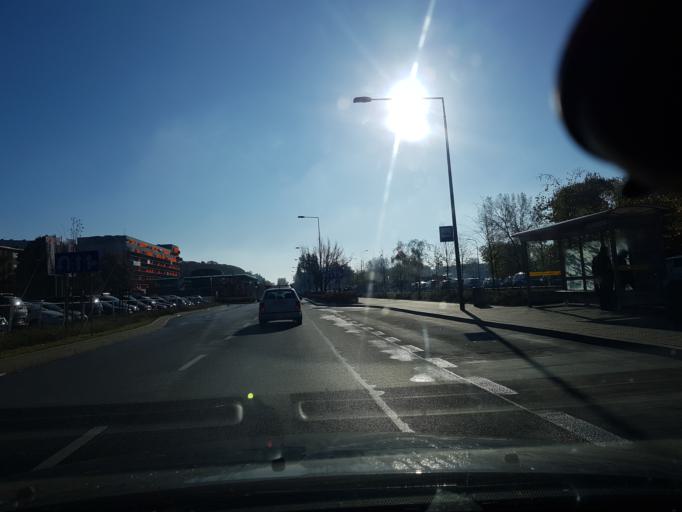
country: PL
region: Masovian Voivodeship
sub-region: Warszawa
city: Bielany
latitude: 52.2874
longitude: 20.9367
